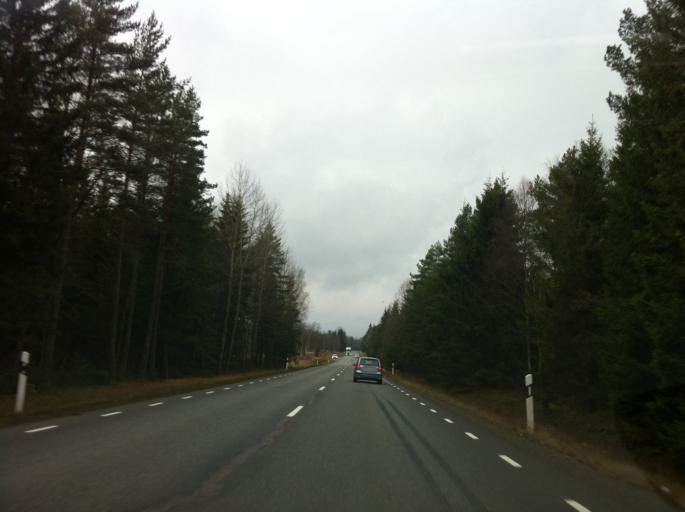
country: SE
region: Joenkoeping
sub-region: Vetlanda Kommun
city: Landsbro
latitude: 57.4070
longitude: 14.9691
